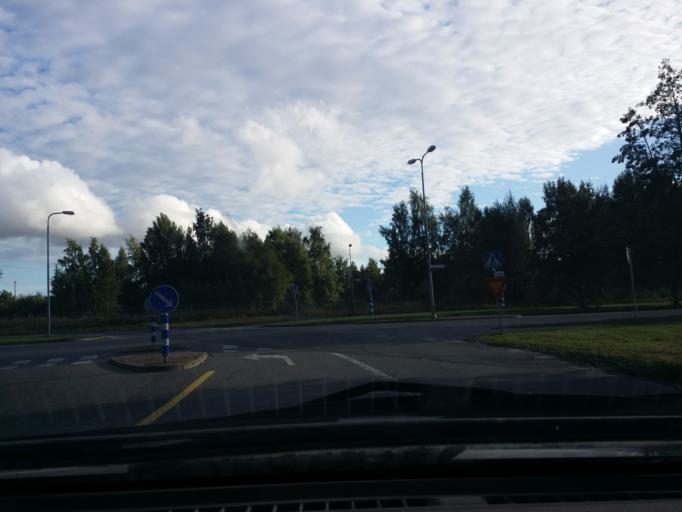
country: FI
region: Satakunta
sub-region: Pori
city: Pori
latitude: 61.4891
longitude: 21.7728
